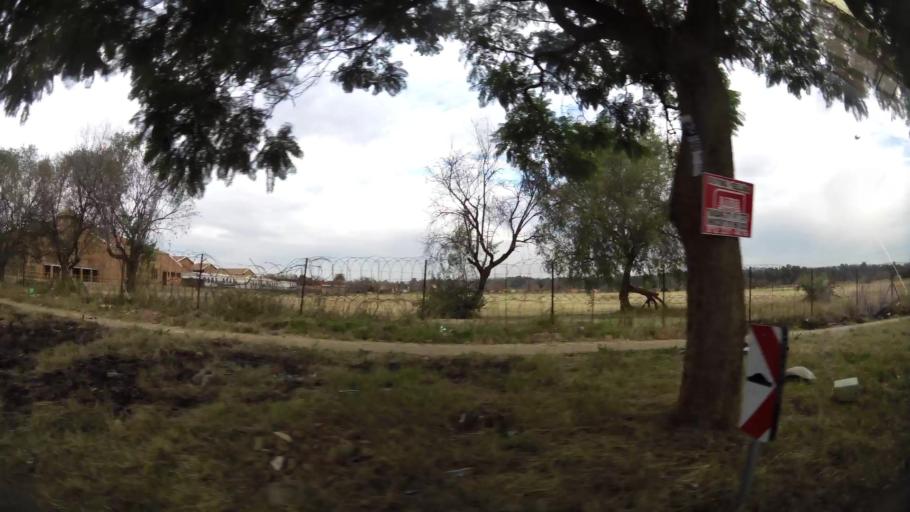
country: ZA
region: Gauteng
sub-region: City of Tshwane Metropolitan Municipality
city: Pretoria
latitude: -25.7014
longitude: 28.3022
